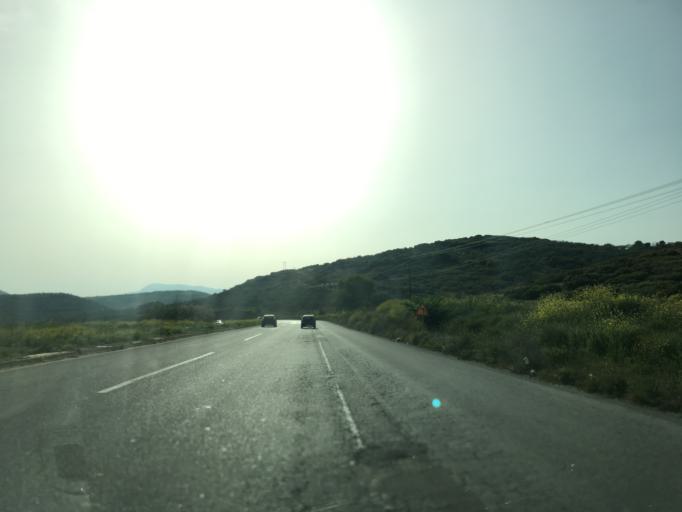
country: GR
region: Thessaly
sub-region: Nomos Magnisias
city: Velestino
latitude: 39.3839
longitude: 22.8377
